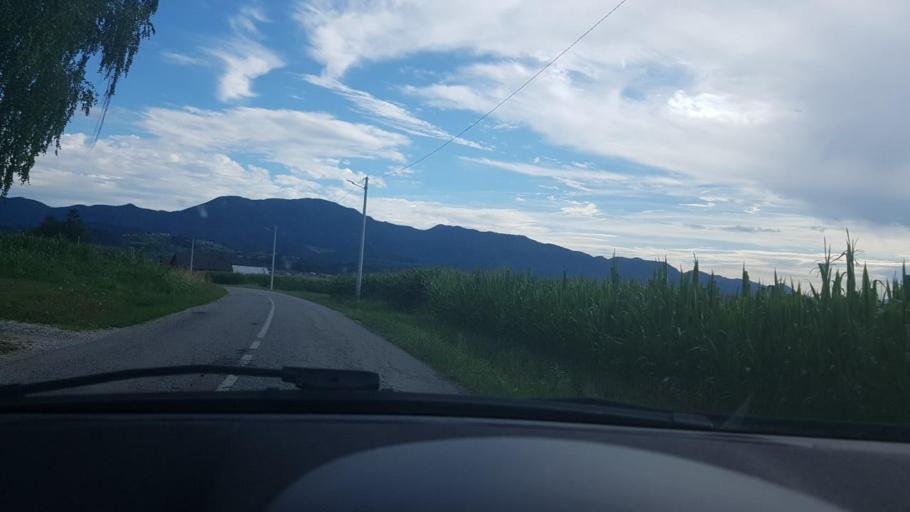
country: HR
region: Varazdinska
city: Tuzno
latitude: 46.2490
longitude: 16.1761
